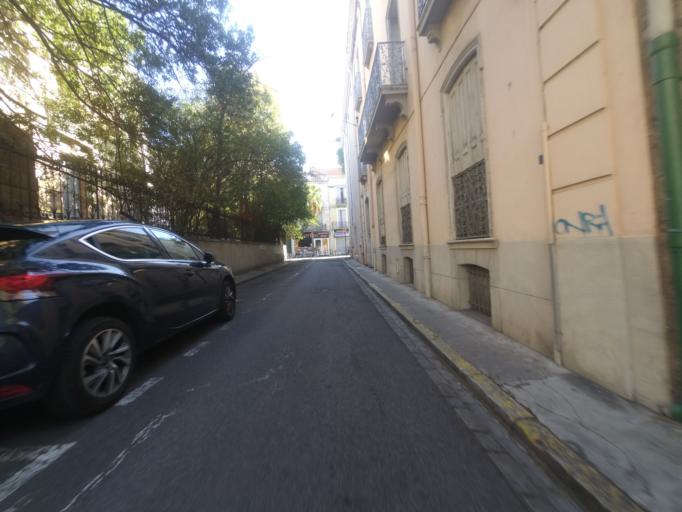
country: FR
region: Languedoc-Roussillon
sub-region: Departement des Pyrenees-Orientales
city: Perpignan
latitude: 42.6973
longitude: 2.8822
